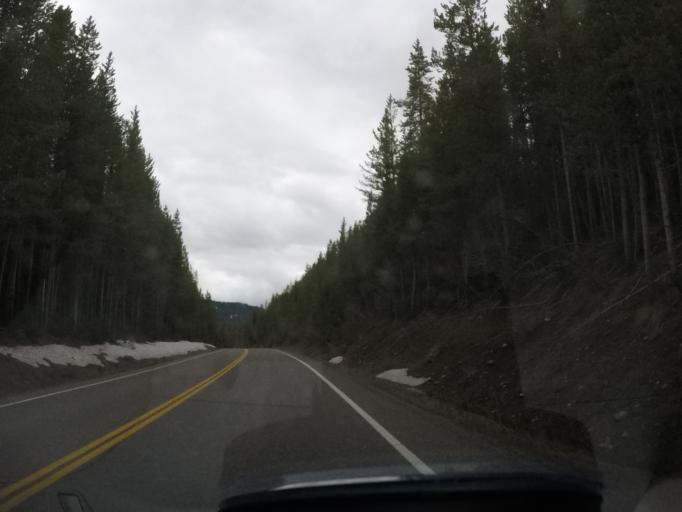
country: US
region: Wyoming
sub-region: Teton County
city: Moose Wilson Road
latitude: 43.9631
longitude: -110.6360
